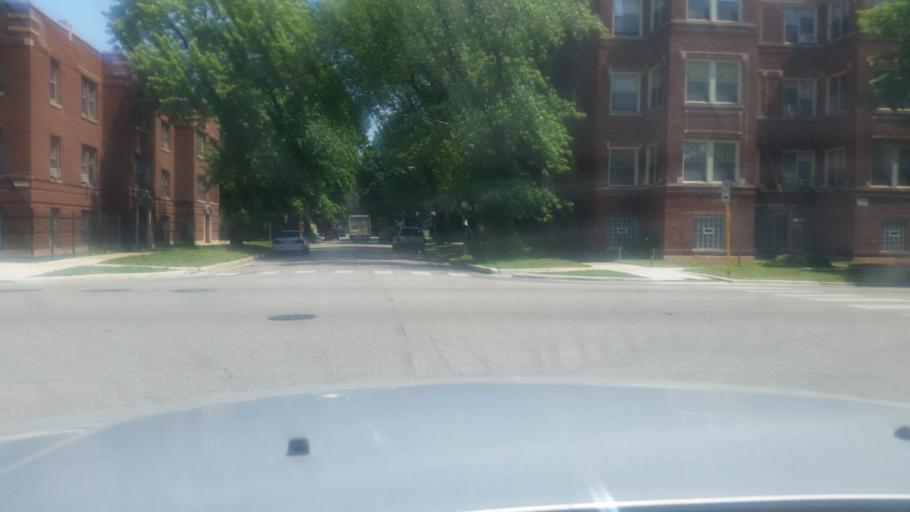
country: US
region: Illinois
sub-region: Cook County
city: Chicago
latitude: 41.7639
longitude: -87.6154
